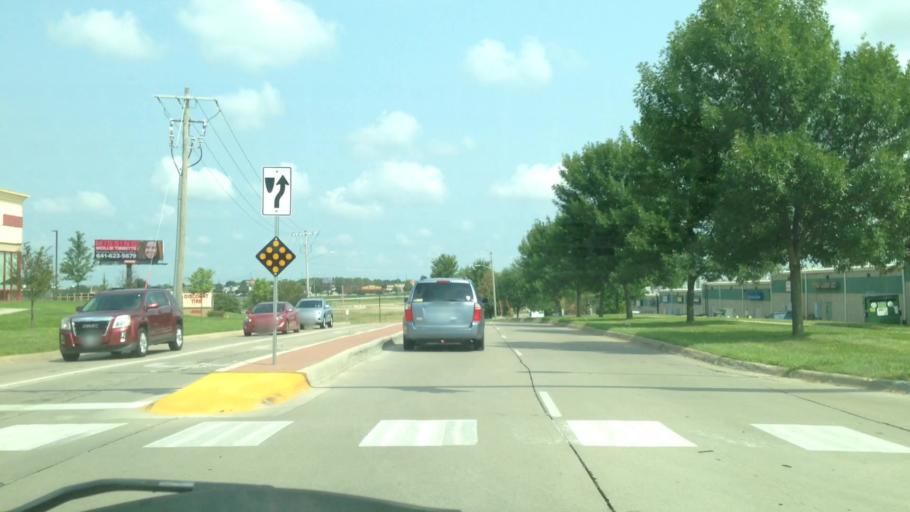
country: US
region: Iowa
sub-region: Linn County
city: Fairfax
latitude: 41.9474
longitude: -91.7210
